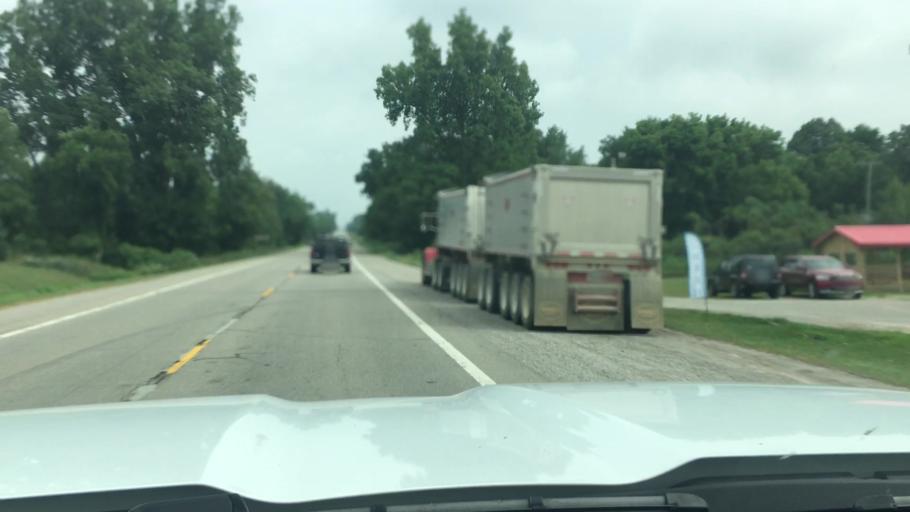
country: US
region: Michigan
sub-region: Sanilac County
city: Brown City
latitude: 43.1536
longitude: -83.0753
